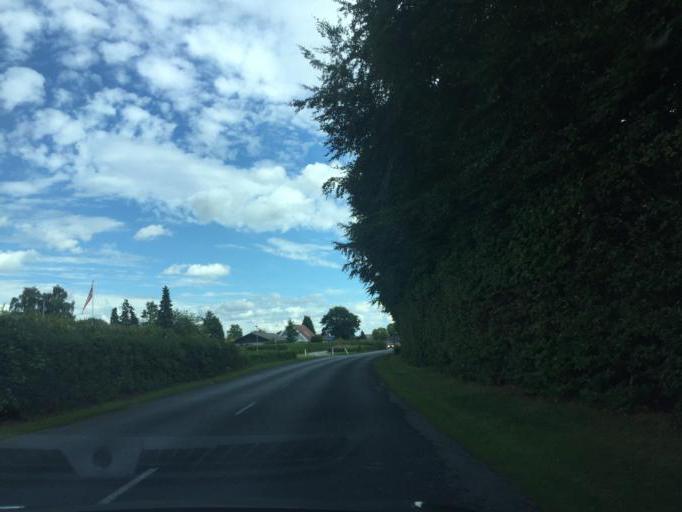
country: DK
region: South Denmark
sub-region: Nordfyns Kommune
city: Otterup
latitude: 55.5178
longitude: 10.3935
